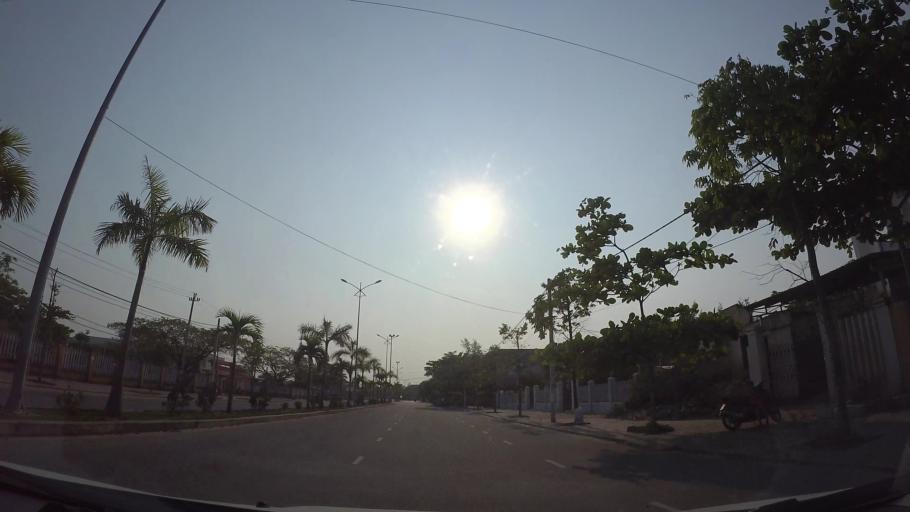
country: VN
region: Da Nang
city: Ngu Hanh Son
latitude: 15.9570
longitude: 108.2576
